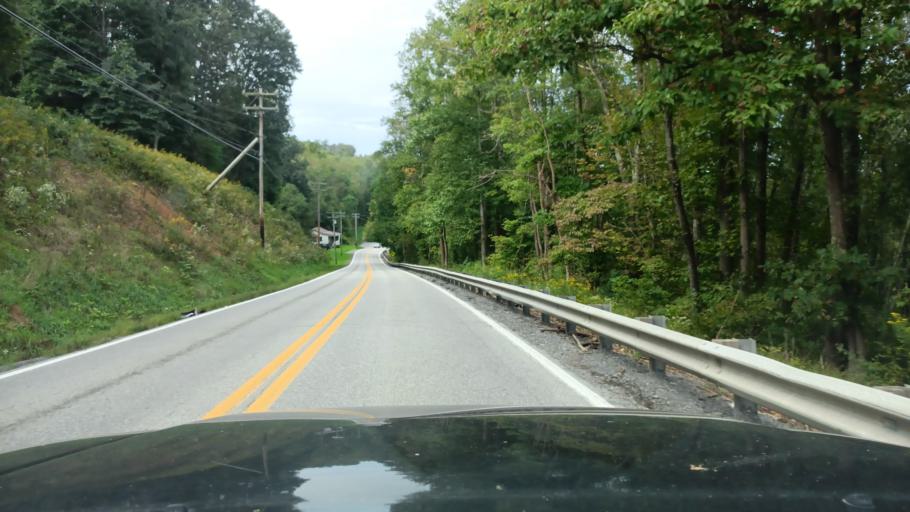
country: US
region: West Virginia
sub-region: Taylor County
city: Grafton
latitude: 39.3444
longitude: -80.0274
